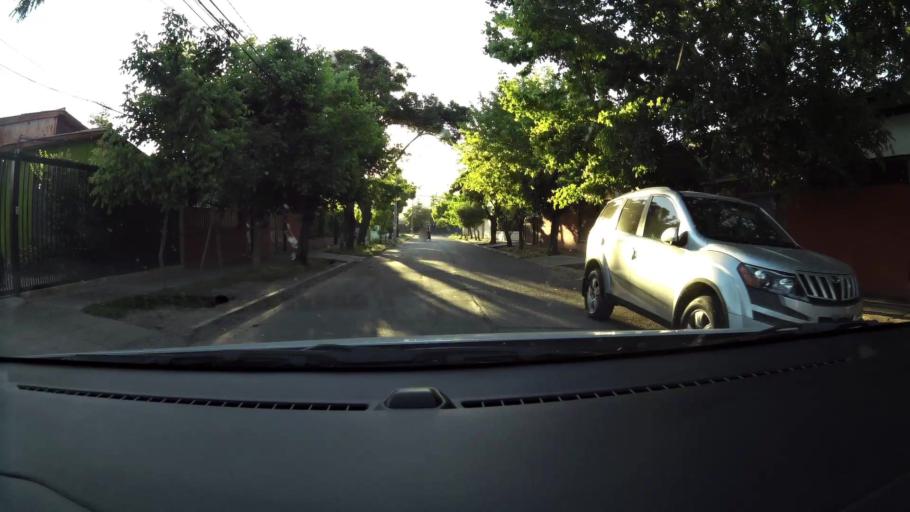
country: CL
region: Santiago Metropolitan
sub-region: Provincia de Maipo
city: San Bernardo
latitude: -33.5915
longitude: -70.6930
